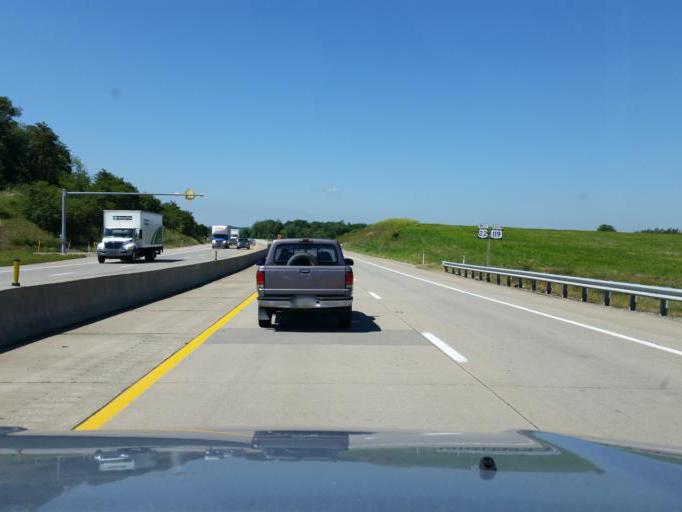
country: US
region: Pennsylvania
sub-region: Westmoreland County
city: Latrobe
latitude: 40.4102
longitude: -79.3945
